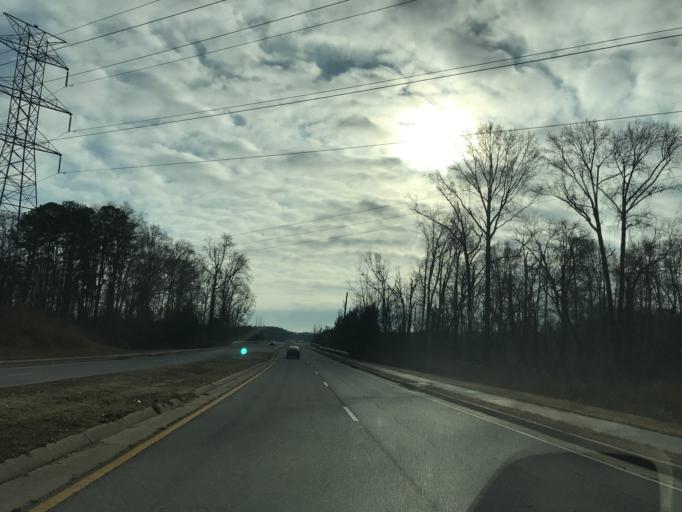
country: US
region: Georgia
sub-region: Clayton County
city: Riverdale
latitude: 33.5913
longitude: -84.4012
